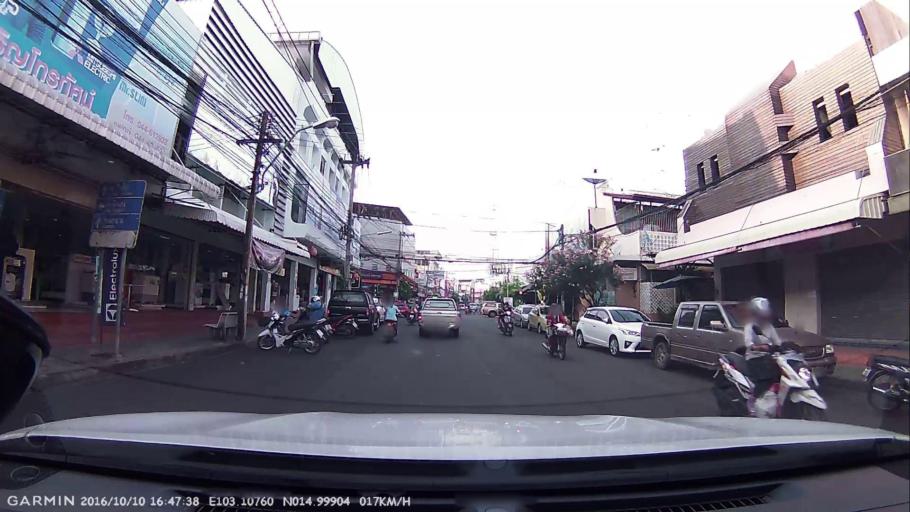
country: TH
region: Buriram
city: Buriram
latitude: 14.9991
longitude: 103.1076
